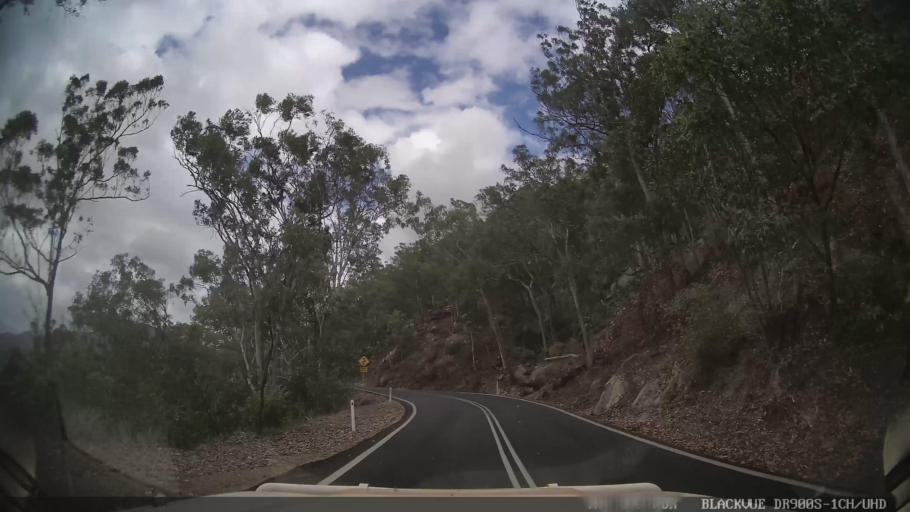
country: AU
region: Queensland
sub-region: Tablelands
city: Tolga
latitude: -17.1837
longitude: 145.6951
